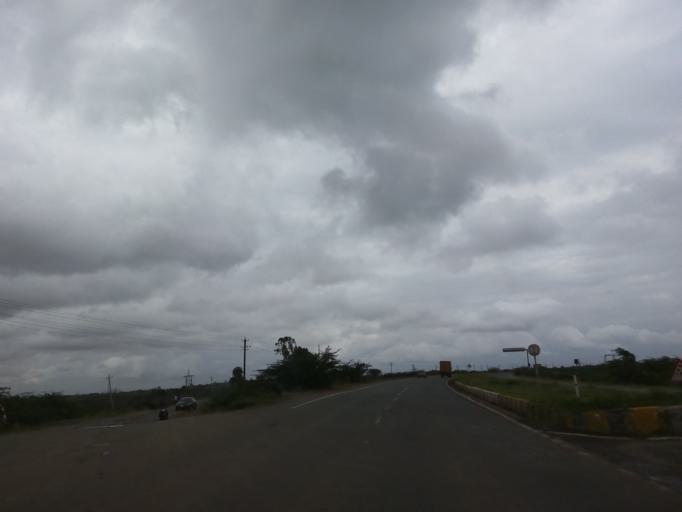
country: IN
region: Karnataka
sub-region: Haveri
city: Ranibennur
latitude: 14.6259
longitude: 75.5994
